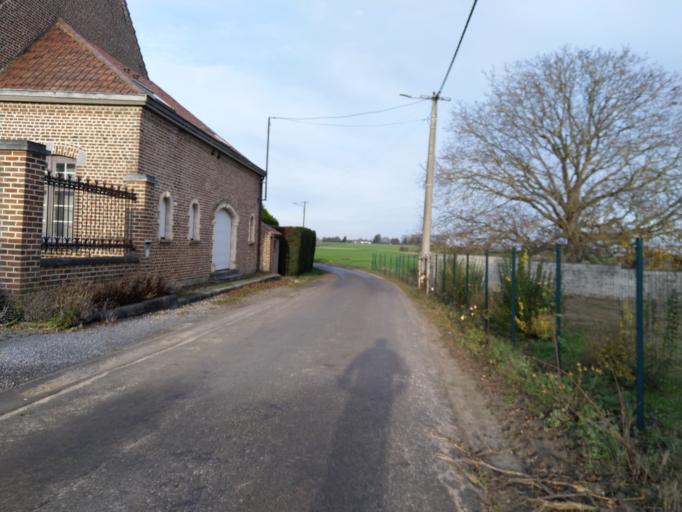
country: BE
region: Wallonia
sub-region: Province du Hainaut
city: Jurbise
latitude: 50.5169
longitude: 3.8434
